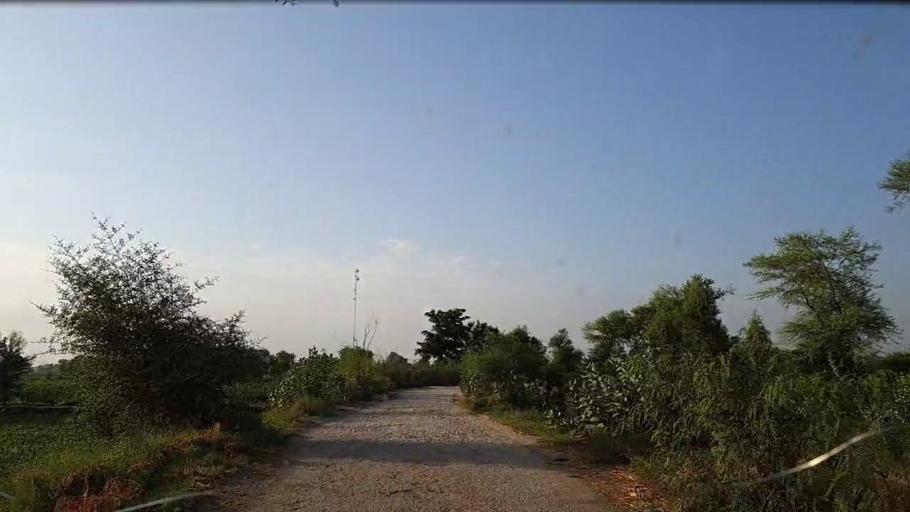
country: PK
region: Sindh
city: Pano Aqil
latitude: 27.9150
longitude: 69.2006
